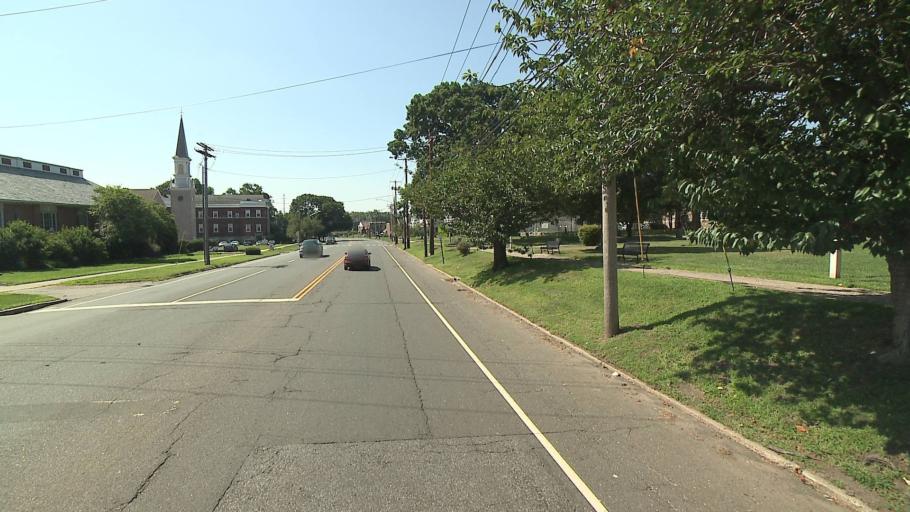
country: US
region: Connecticut
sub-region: Fairfield County
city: Stratford
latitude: 41.1974
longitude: -73.1319
